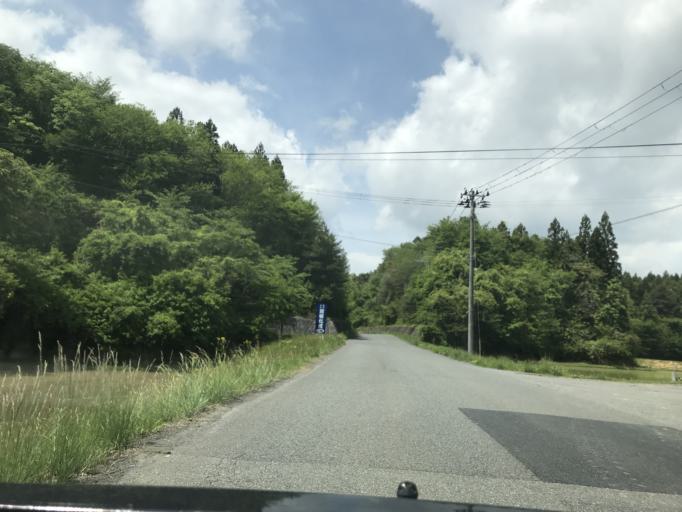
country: JP
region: Miyagi
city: Furukawa
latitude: 38.7719
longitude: 140.9567
